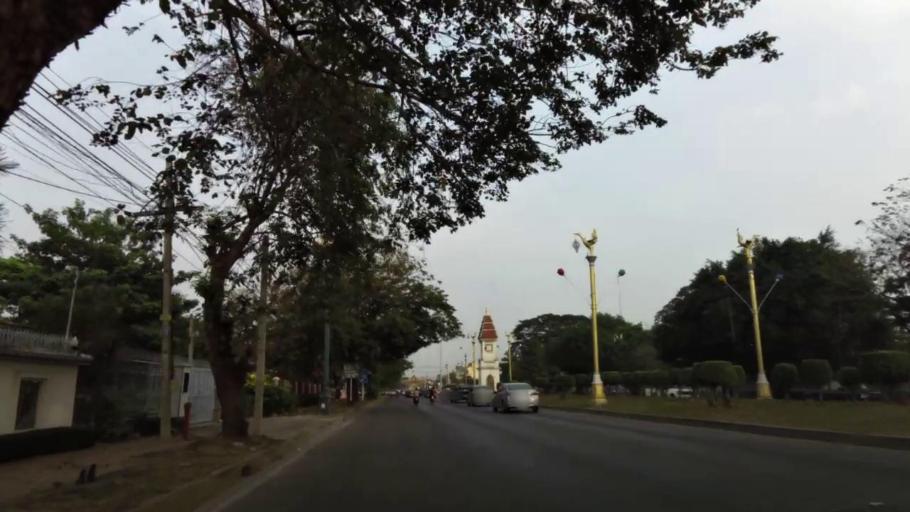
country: TH
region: Phra Nakhon Si Ayutthaya
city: Phra Nakhon Si Ayutthaya
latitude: 14.3514
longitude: 100.5738
